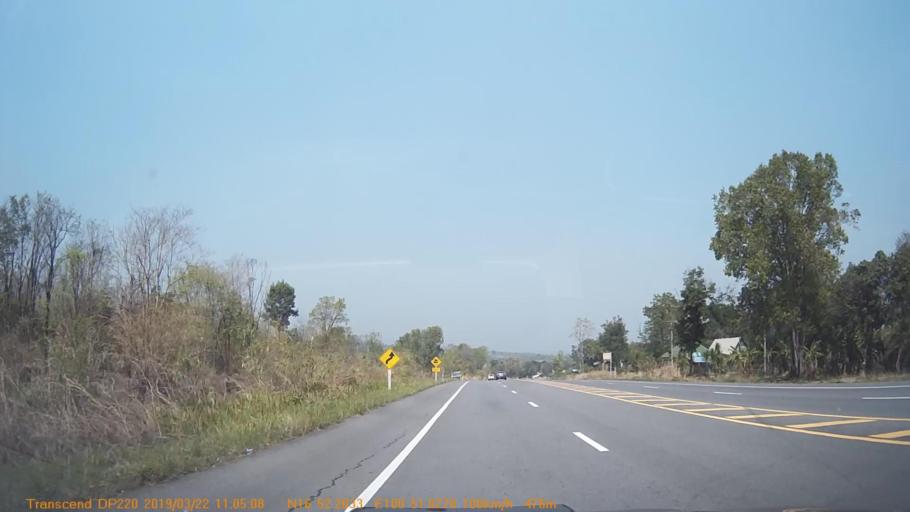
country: TH
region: Phitsanulok
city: Nakhon Thai
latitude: 16.8716
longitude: 100.8501
